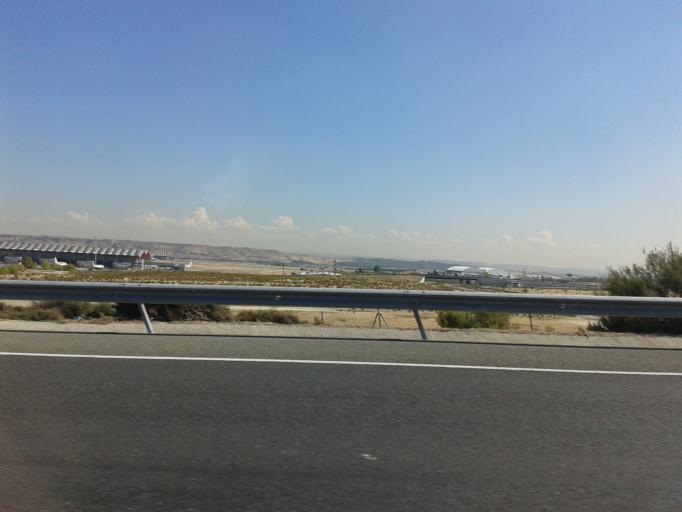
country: ES
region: Madrid
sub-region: Provincia de Madrid
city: Barajas de Madrid
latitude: 40.4839
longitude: -3.6012
